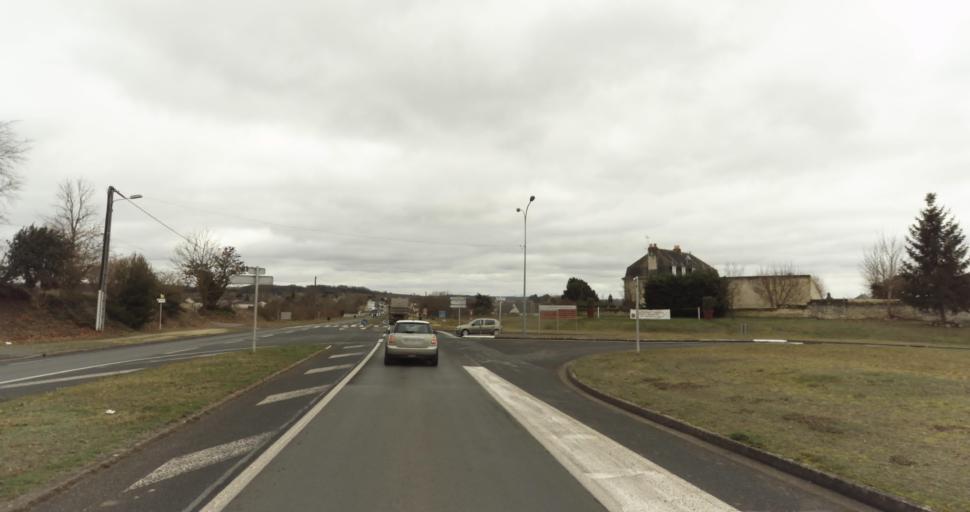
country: FR
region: Pays de la Loire
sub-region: Departement de Maine-et-Loire
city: Varrains
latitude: 47.2257
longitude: -0.0657
